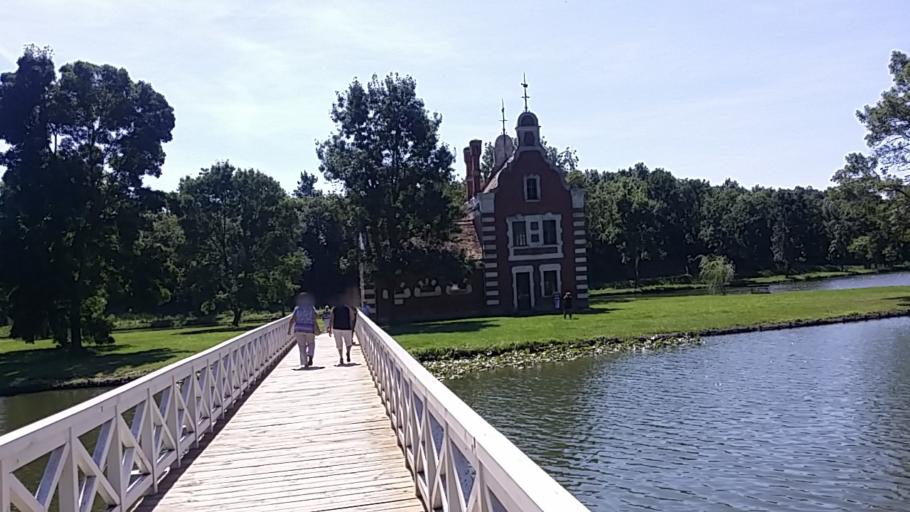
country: HU
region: Fejer
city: Deg
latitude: 46.8720
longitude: 18.4360
